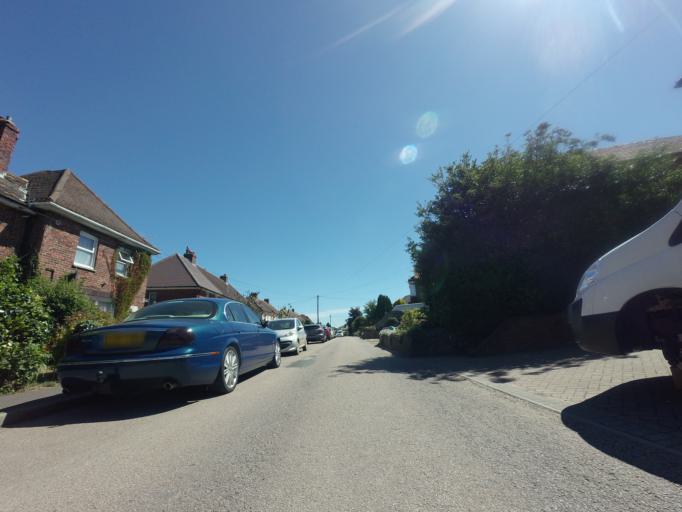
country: GB
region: England
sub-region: Kent
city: Eastry
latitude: 51.2438
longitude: 1.3007
